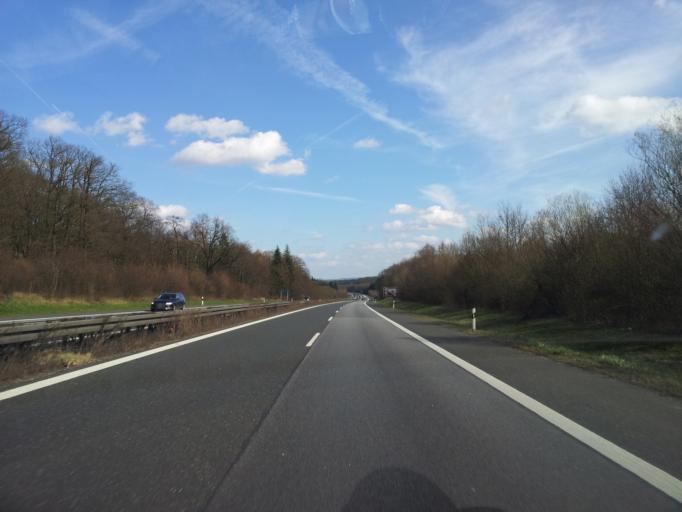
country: DE
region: Bavaria
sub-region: Regierungsbezirk Unterfranken
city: Gadheim
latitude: 50.0065
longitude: 10.3826
